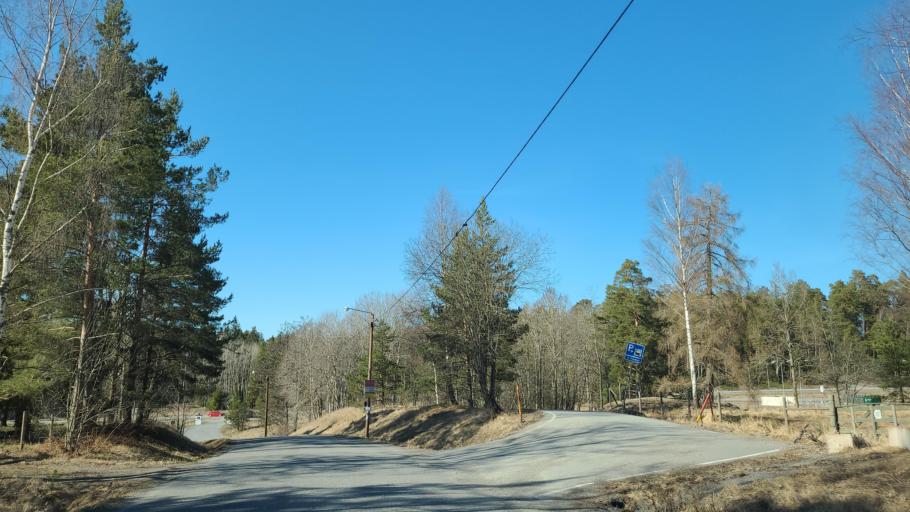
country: SE
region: Stockholm
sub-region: Varmdo Kommun
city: Hemmesta
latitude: 59.2808
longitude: 18.5697
